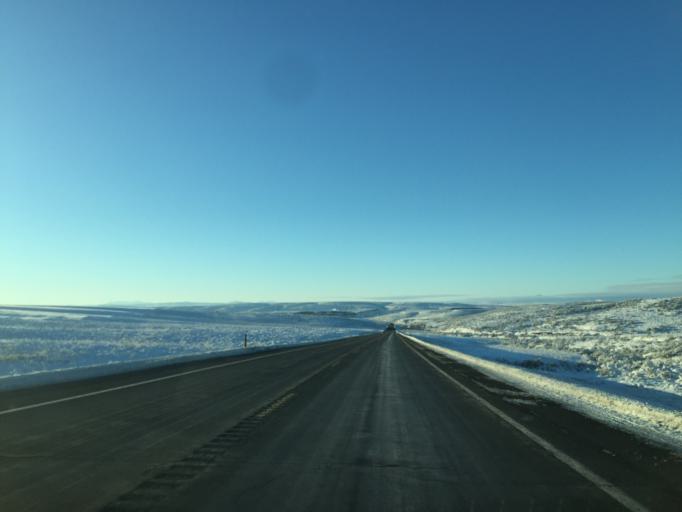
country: US
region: Washington
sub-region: Grant County
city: Soap Lake
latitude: 47.5999
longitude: -119.6115
